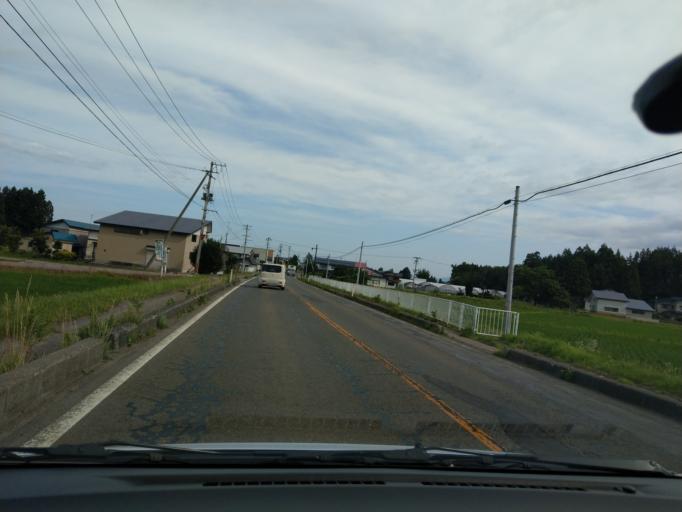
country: JP
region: Akita
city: Yokotemachi
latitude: 39.3941
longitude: 140.5663
